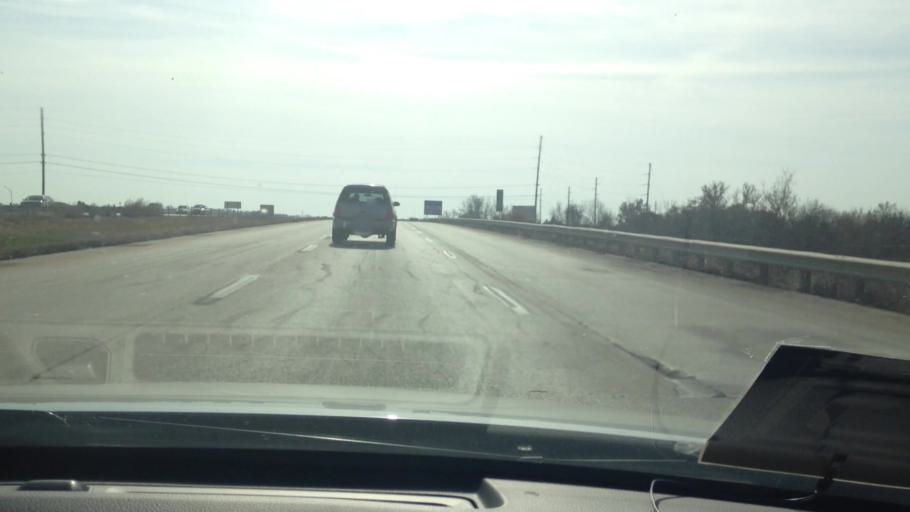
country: US
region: Missouri
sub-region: Cass County
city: Harrisonville
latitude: 38.6573
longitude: -94.3670
